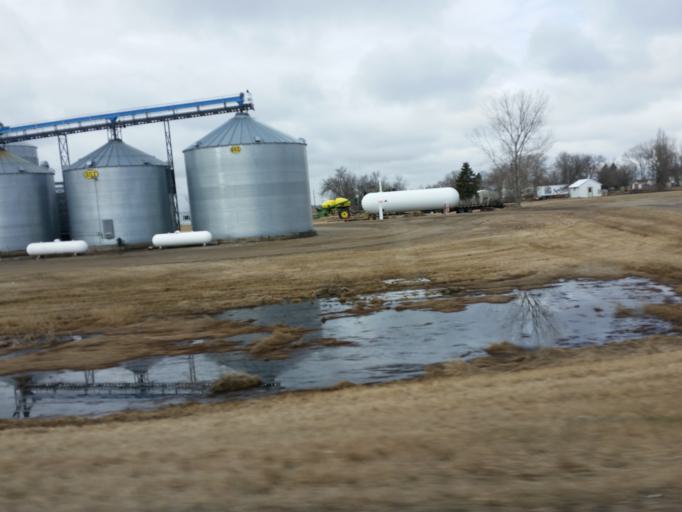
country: US
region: North Dakota
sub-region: Traill County
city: Hillsboro
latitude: 47.3440
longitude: -97.2177
